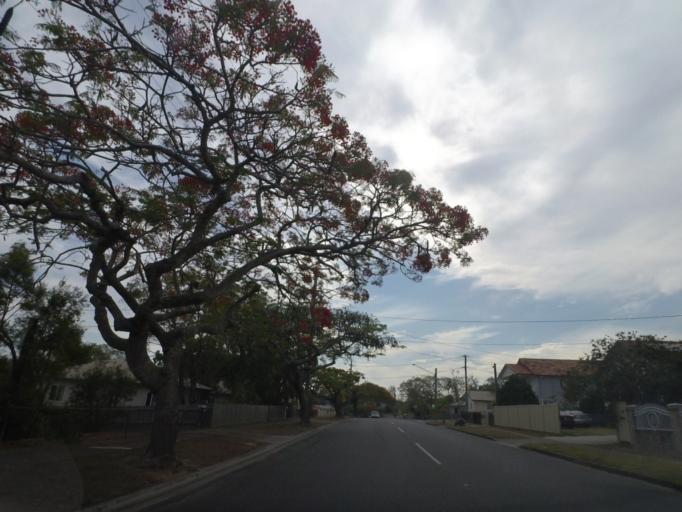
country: AU
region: Queensland
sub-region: Brisbane
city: Inala
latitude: -27.5911
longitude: 152.9652
